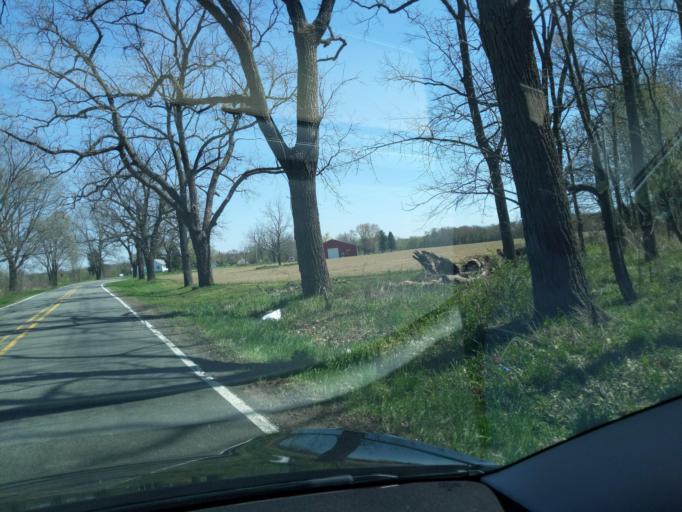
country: US
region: Michigan
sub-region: Ingham County
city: Stockbridge
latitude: 42.4959
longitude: -84.2266
